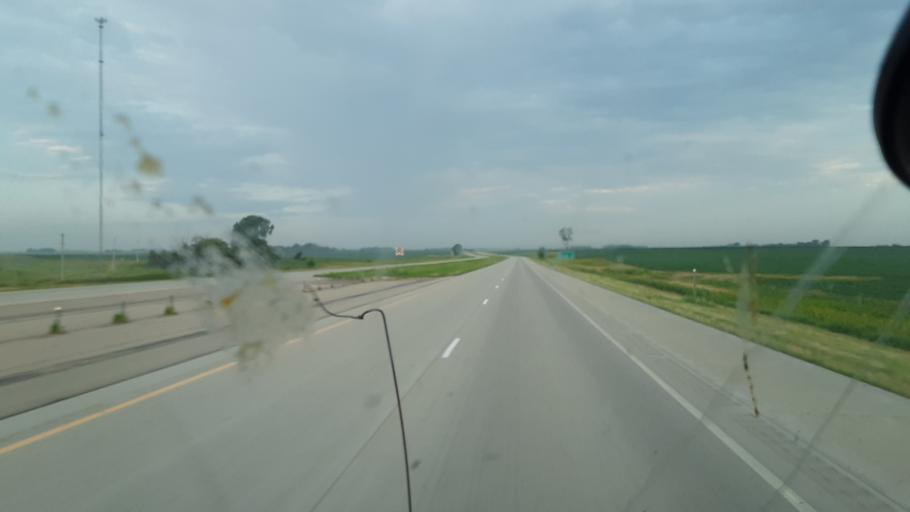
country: US
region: Minnesota
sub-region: Faribault County
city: Wells
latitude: 43.6664
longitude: -93.5913
